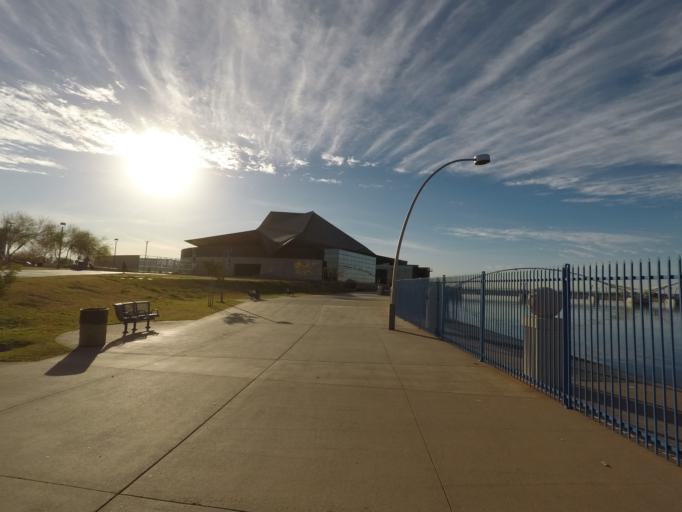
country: US
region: Arizona
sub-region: Maricopa County
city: Tempe Junction
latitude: 33.4323
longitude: -111.9472
